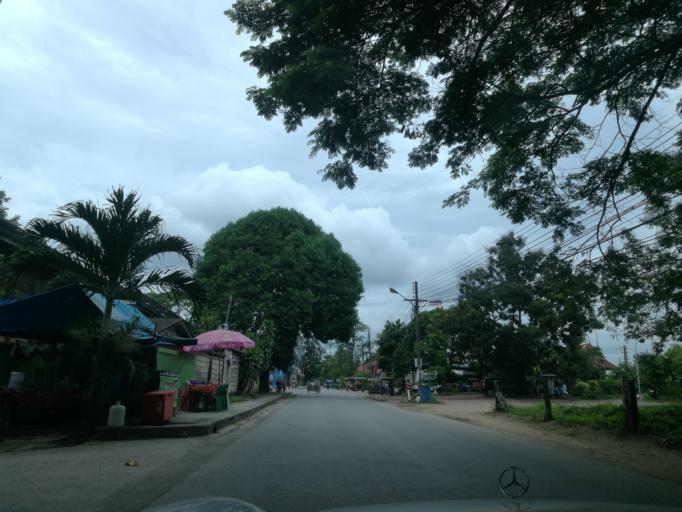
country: TH
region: Prachuap Khiri Khan
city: Prachuap Khiri Khan
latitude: 11.8087
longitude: 99.7938
